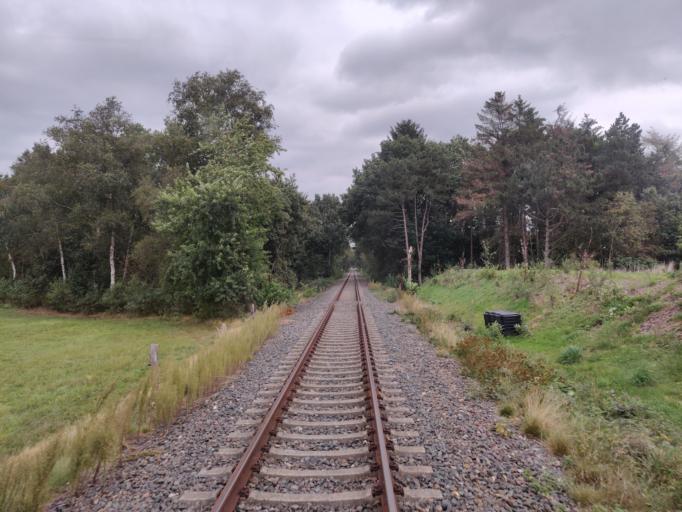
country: DE
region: Lower Saxony
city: Worpswede
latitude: 53.2315
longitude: 8.9345
